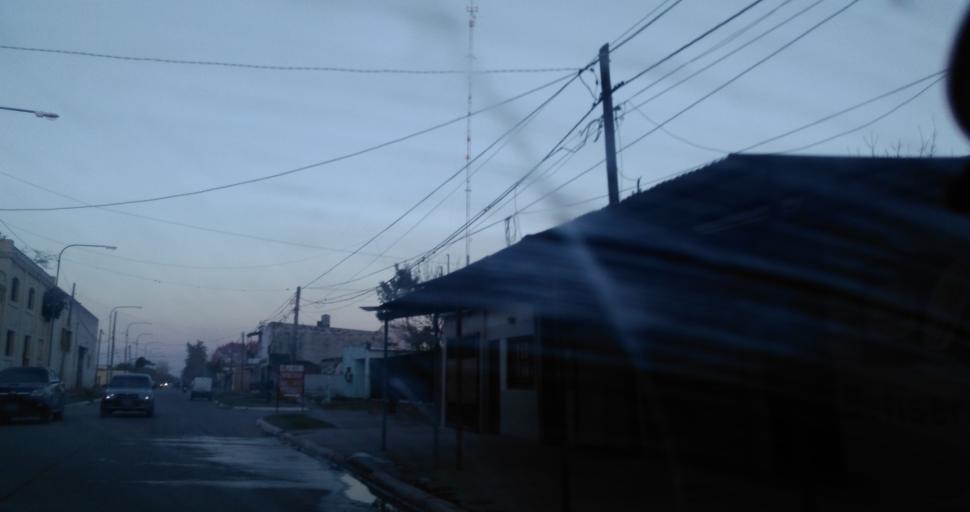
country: AR
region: Chaco
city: Resistencia
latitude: -27.4733
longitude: -58.9619
